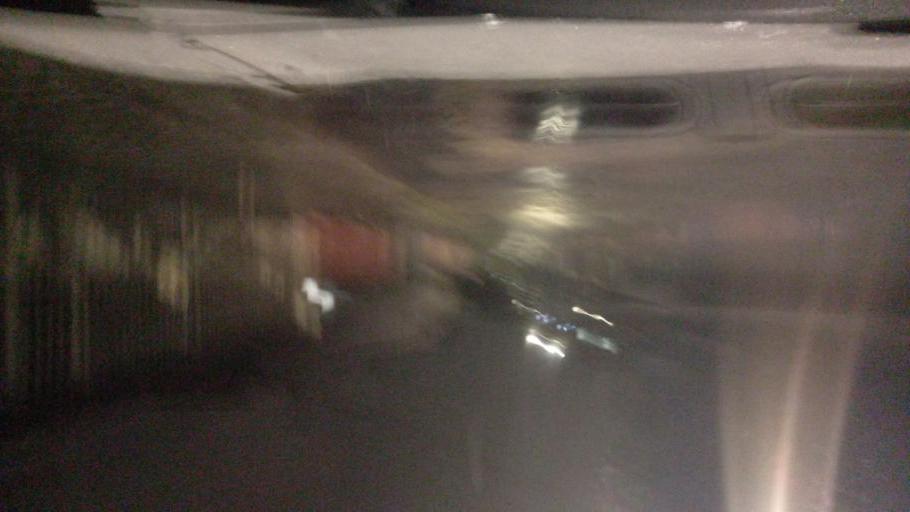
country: BR
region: Minas Gerais
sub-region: Belo Horizonte
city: Belo Horizonte
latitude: -19.9141
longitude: -43.9699
